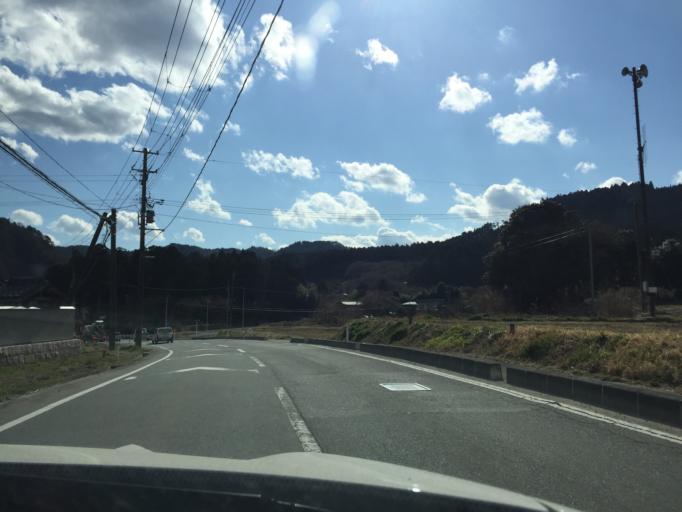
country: JP
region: Fukushima
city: Namie
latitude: 37.2800
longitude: 140.9767
